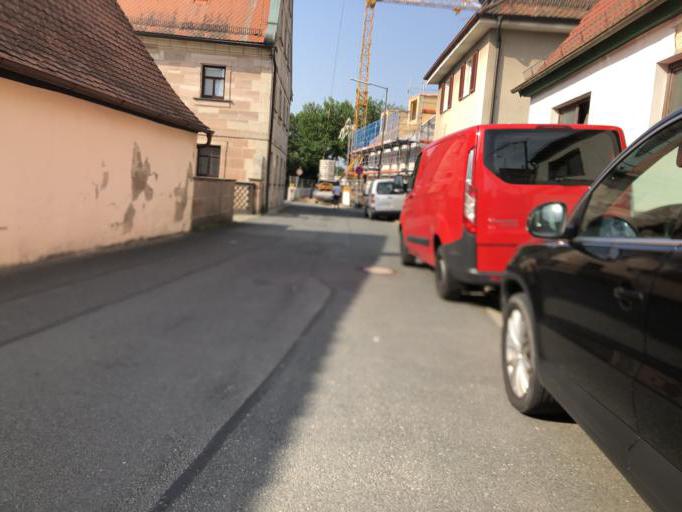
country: DE
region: Bavaria
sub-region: Regierungsbezirk Mittelfranken
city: Erlangen
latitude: 49.5502
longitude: 11.0290
